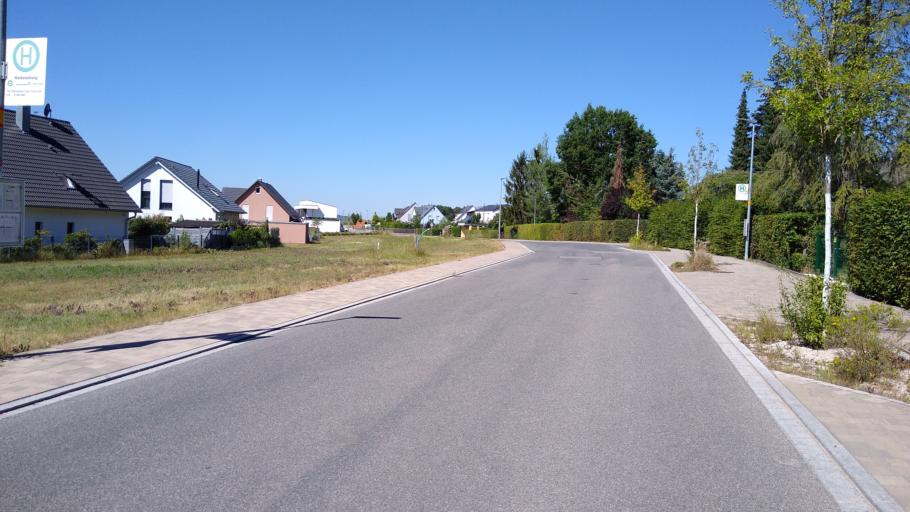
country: DE
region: Bavaria
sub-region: Regierungsbezirk Mittelfranken
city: Seukendorf
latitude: 49.4679
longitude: 10.8894
